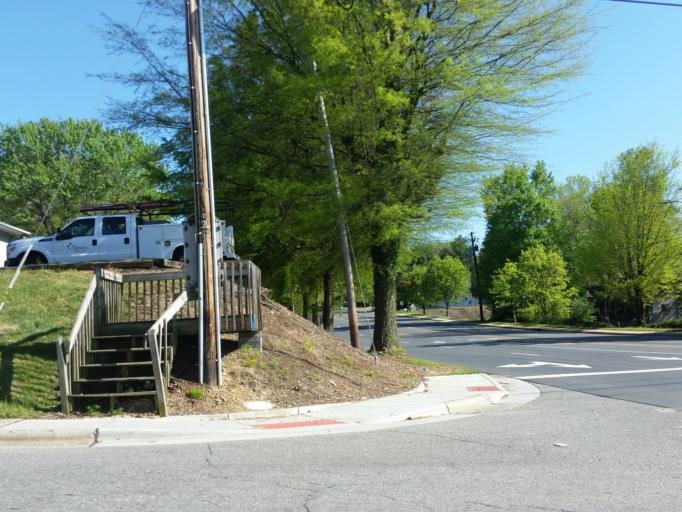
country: US
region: North Carolina
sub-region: Buncombe County
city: Asheville
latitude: 35.5817
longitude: -82.5541
